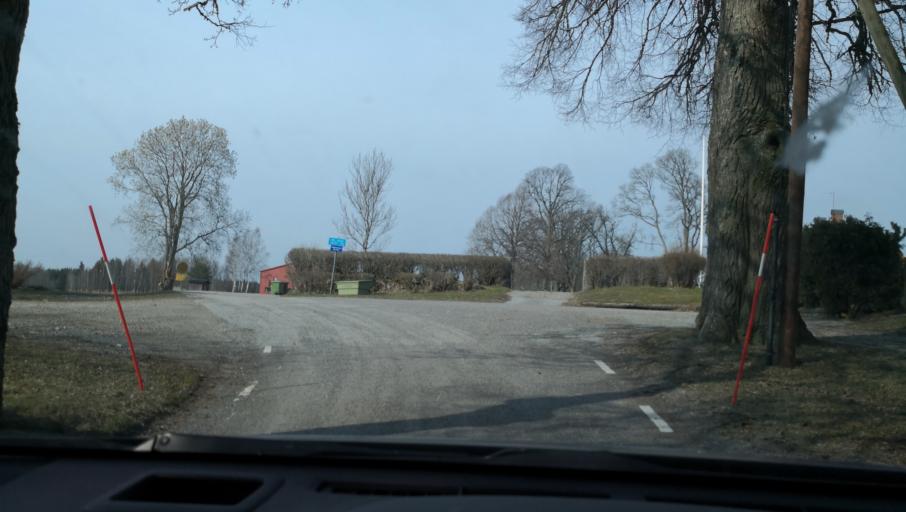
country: SE
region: OErebro
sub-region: Lindesbergs Kommun
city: Frovi
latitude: 59.4074
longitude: 15.4155
